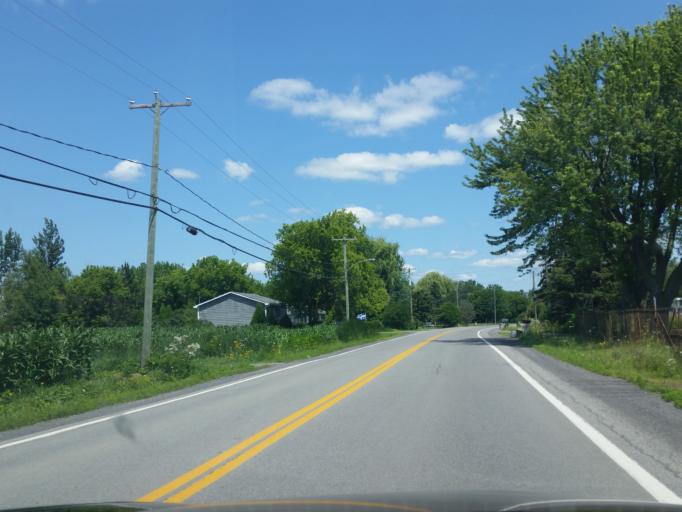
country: CA
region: Quebec
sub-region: Monteregie
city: Richelieu
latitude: 45.3988
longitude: -73.2604
